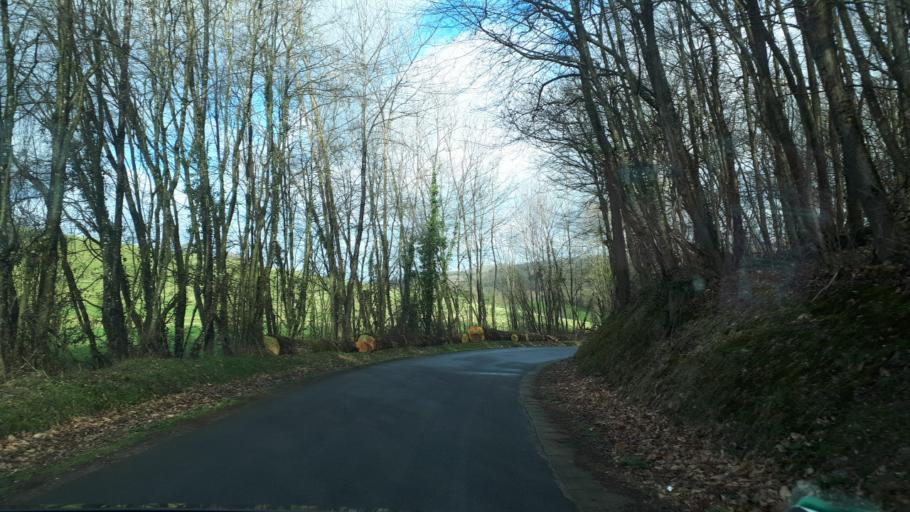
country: FR
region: Centre
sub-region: Departement du Loir-et-Cher
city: Sarge-sur-Braye
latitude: 47.9093
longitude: 0.8709
